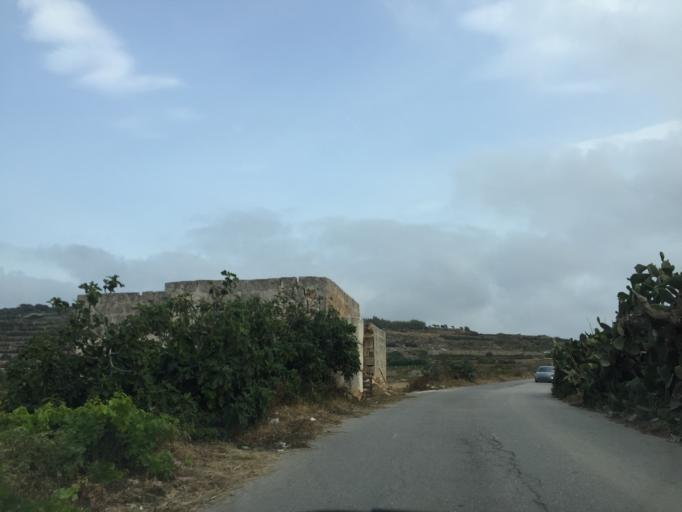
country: MT
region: L-Imgarr
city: Imgarr
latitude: 35.9345
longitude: 14.3514
